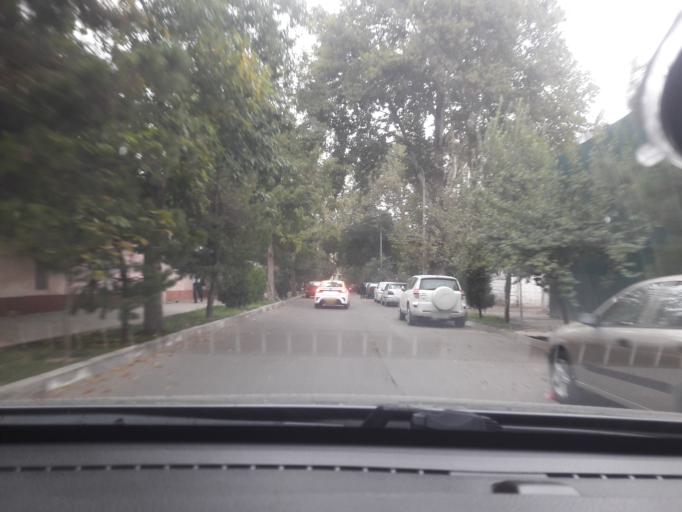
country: TJ
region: Dushanbe
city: Dushanbe
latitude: 38.5658
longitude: 68.7922
